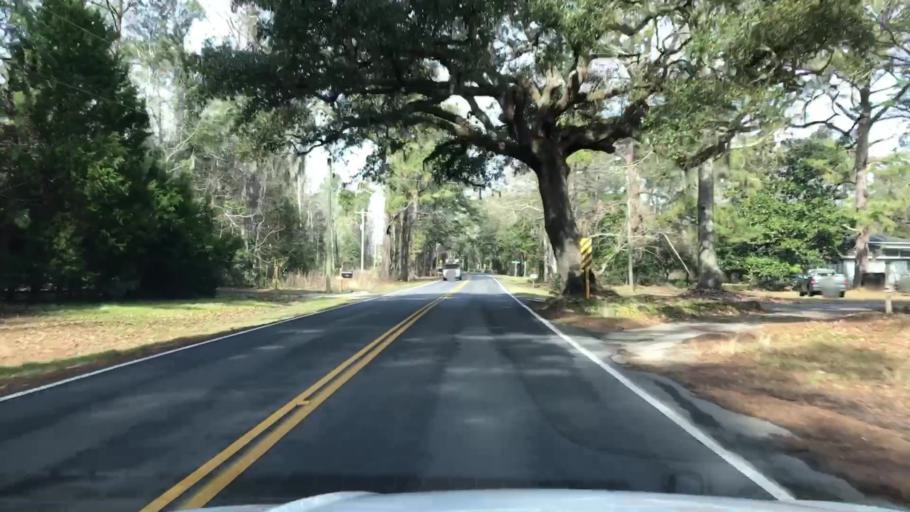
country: US
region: South Carolina
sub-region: Charleston County
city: Folly Beach
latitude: 32.7141
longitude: -80.0191
